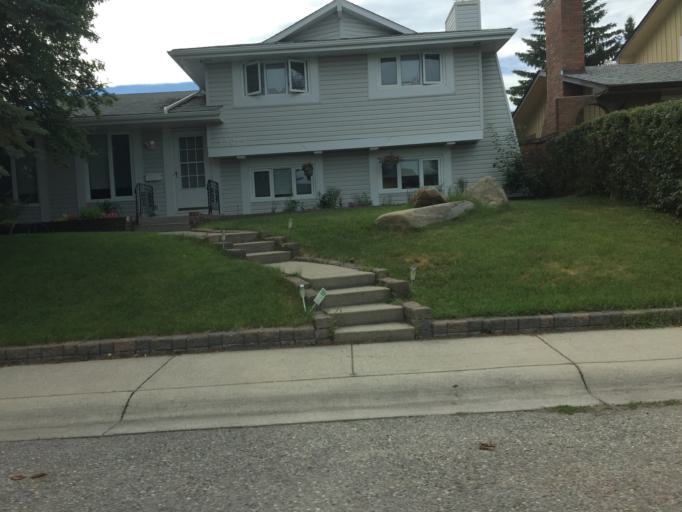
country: CA
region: Alberta
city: Calgary
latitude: 50.9356
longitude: -114.0389
